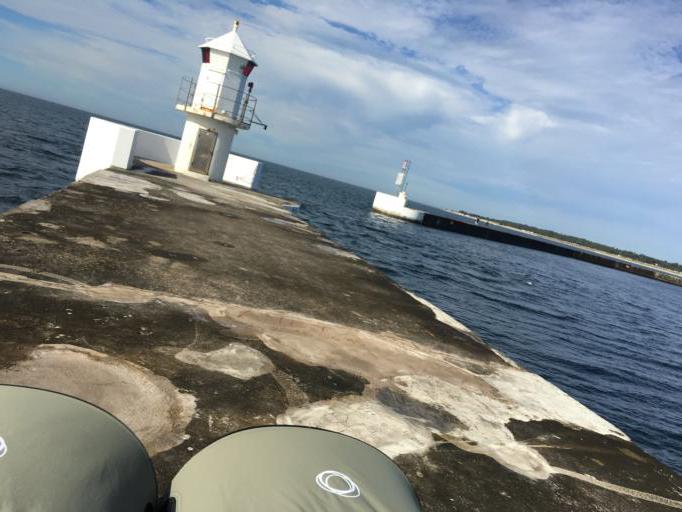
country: SE
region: Skane
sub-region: Vellinge Kommun
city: Hollviken
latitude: 55.3932
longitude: 12.9499
